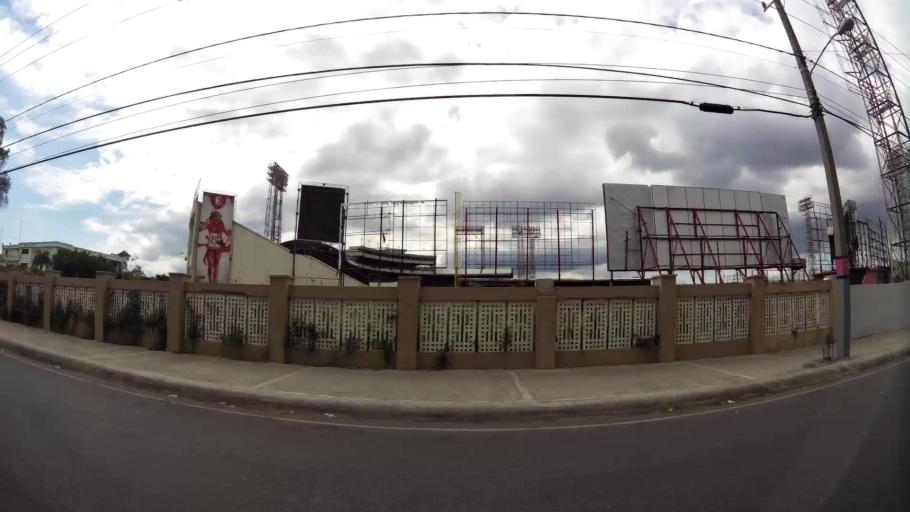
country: DO
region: Nacional
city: La Agustina
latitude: 18.4882
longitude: -69.9251
